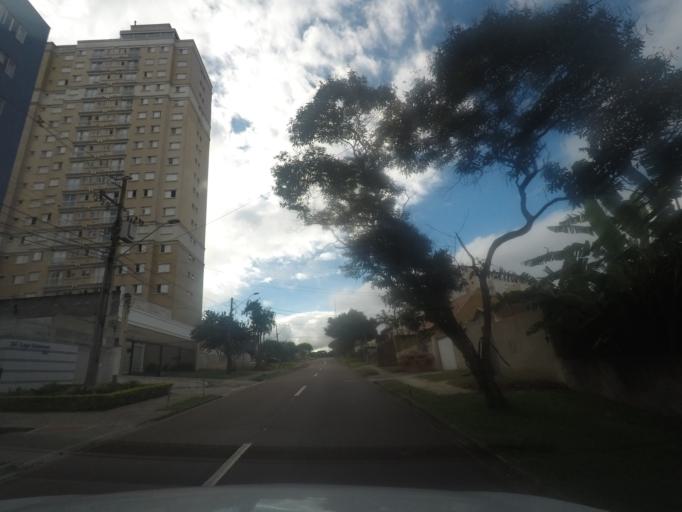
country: BR
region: Parana
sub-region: Curitiba
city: Curitiba
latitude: -25.4359
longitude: -49.2374
